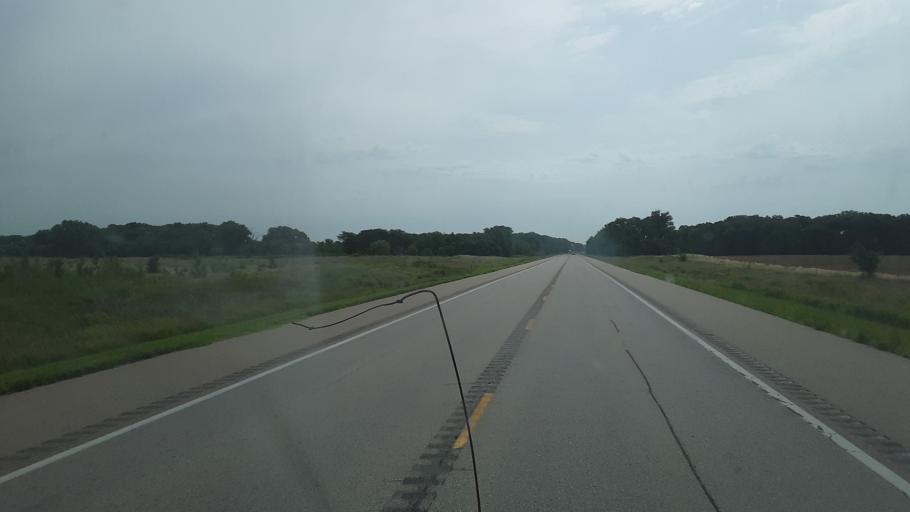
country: US
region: Kansas
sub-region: Stafford County
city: Stafford
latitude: 37.9844
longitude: -98.3793
